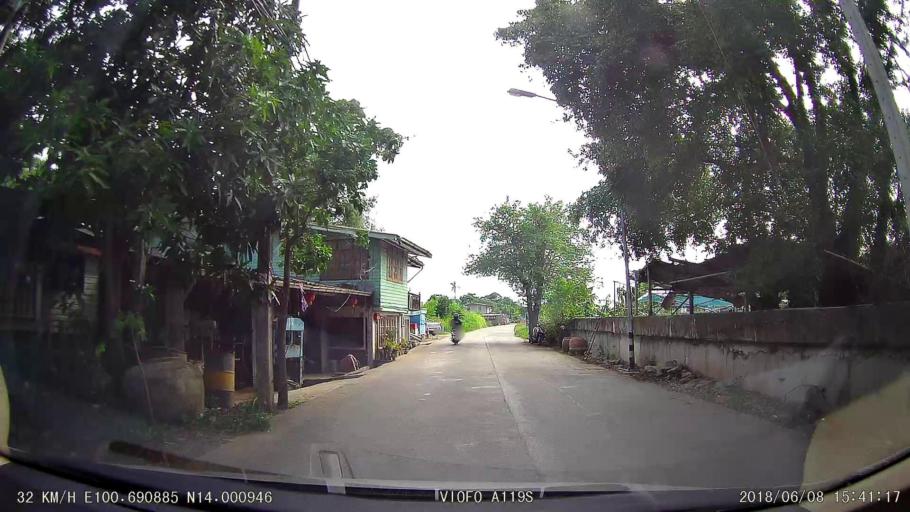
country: TH
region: Pathum Thani
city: Thanyaburi
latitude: 14.0009
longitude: 100.6908
